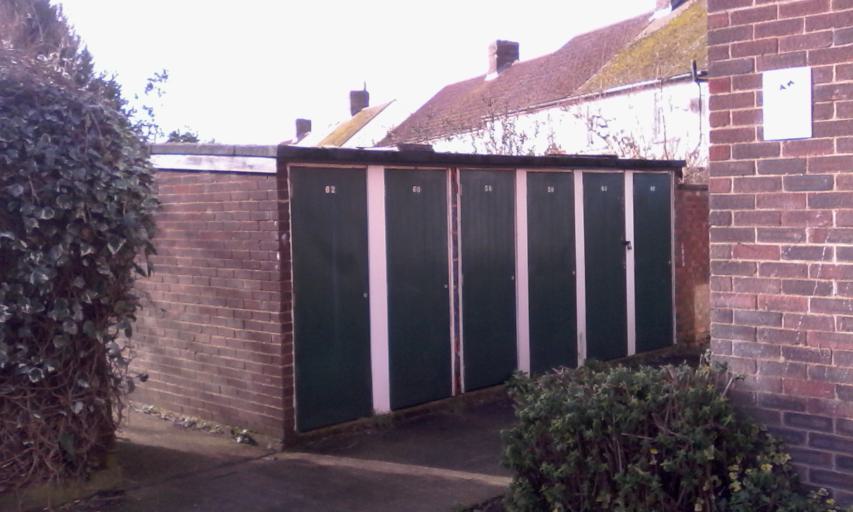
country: GB
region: England
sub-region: Hertfordshire
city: Ware
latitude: 51.8169
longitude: -0.0224
